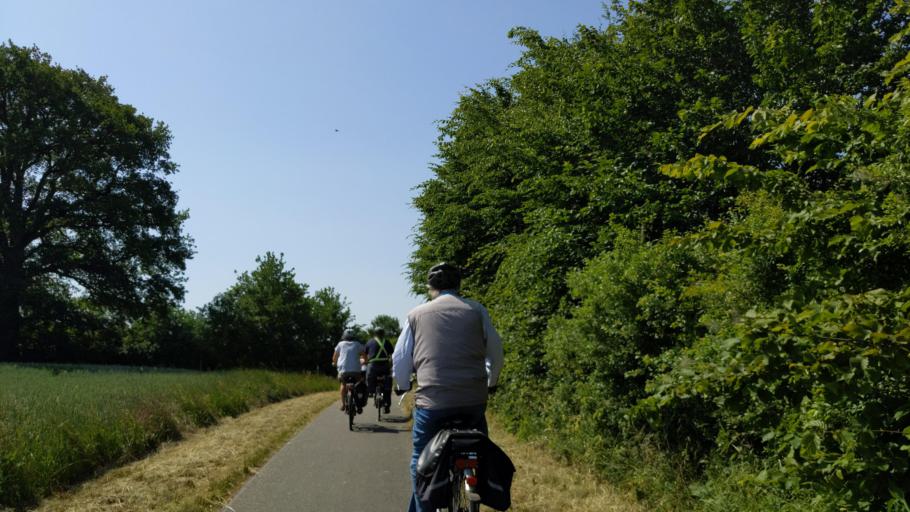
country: DE
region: Schleswig-Holstein
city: Berkenthin
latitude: 53.7394
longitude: 10.6545
